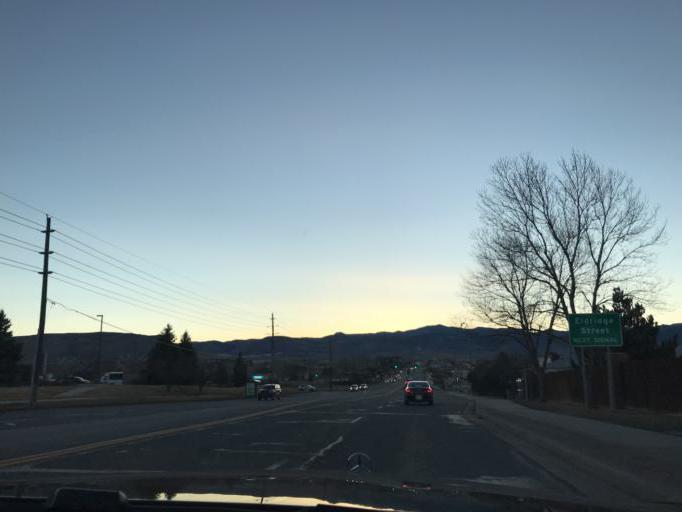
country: US
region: Colorado
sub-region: Jefferson County
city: Applewood
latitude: 39.8127
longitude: -105.1549
